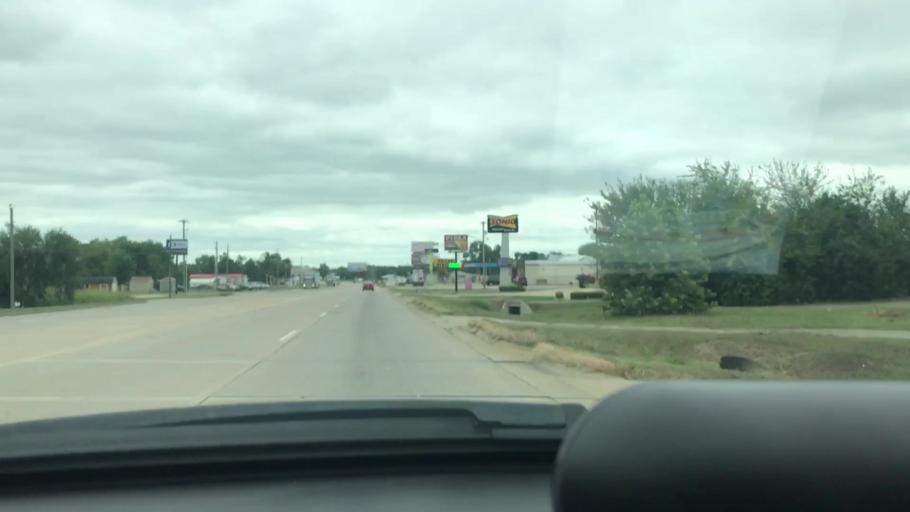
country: US
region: Oklahoma
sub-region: Mayes County
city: Chouteau
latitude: 36.1709
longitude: -95.3419
